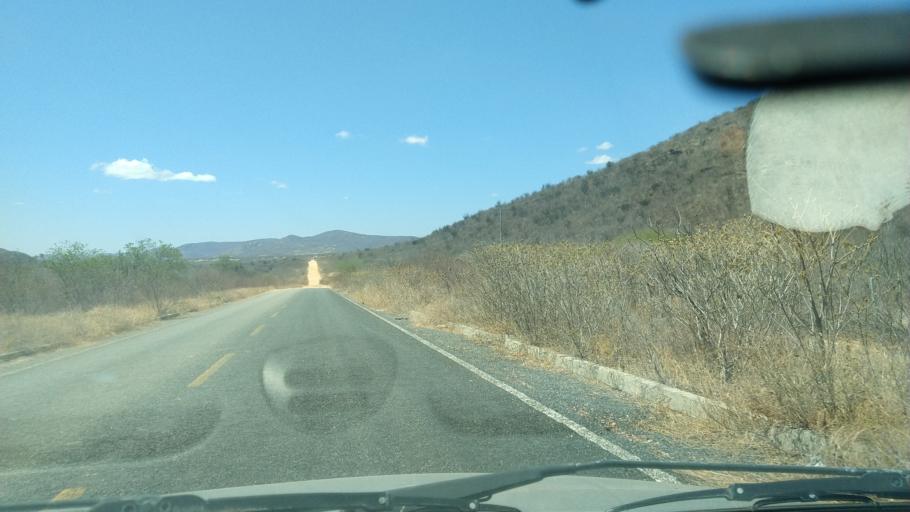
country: BR
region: Rio Grande do Norte
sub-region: Sao Tome
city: Sao Tome
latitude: -5.9682
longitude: -36.1598
